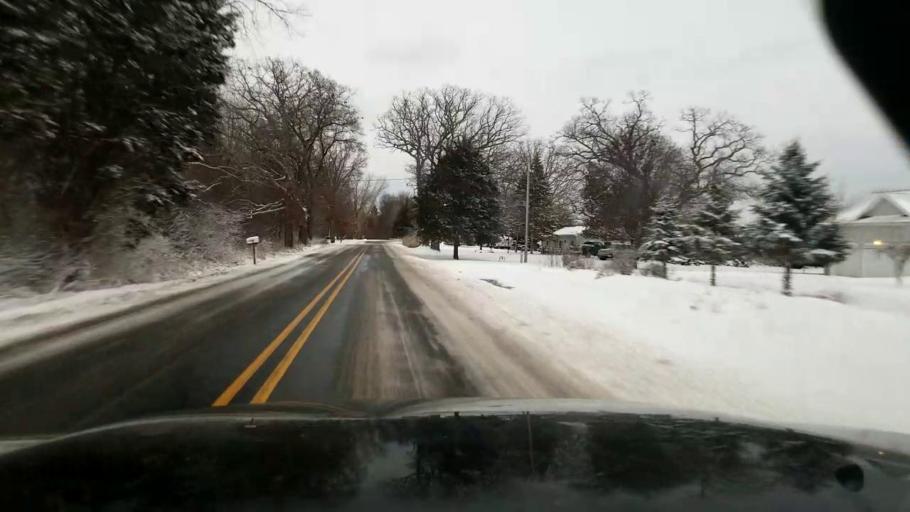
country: US
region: Michigan
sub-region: Jackson County
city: Spring Arbor
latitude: 42.0976
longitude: -84.4797
